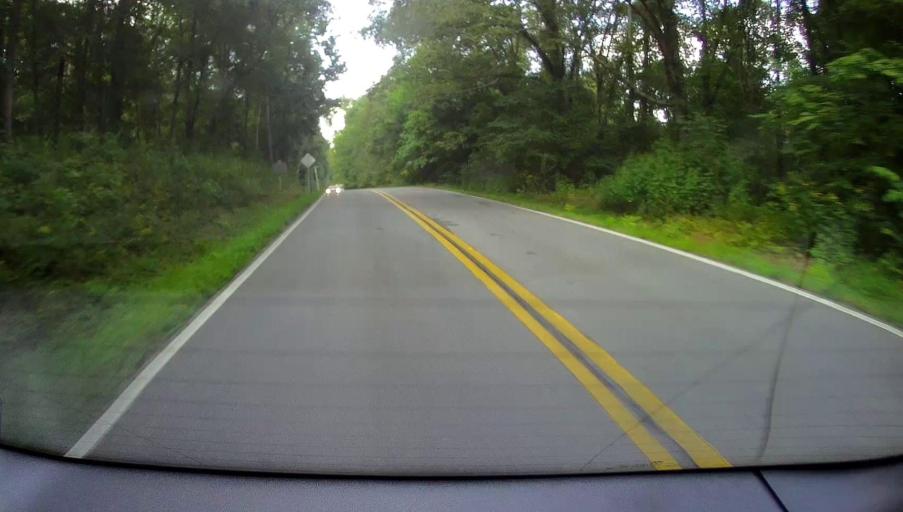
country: US
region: Georgia
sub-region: Catoosa County
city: Ringgold
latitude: 34.9162
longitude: -85.0862
